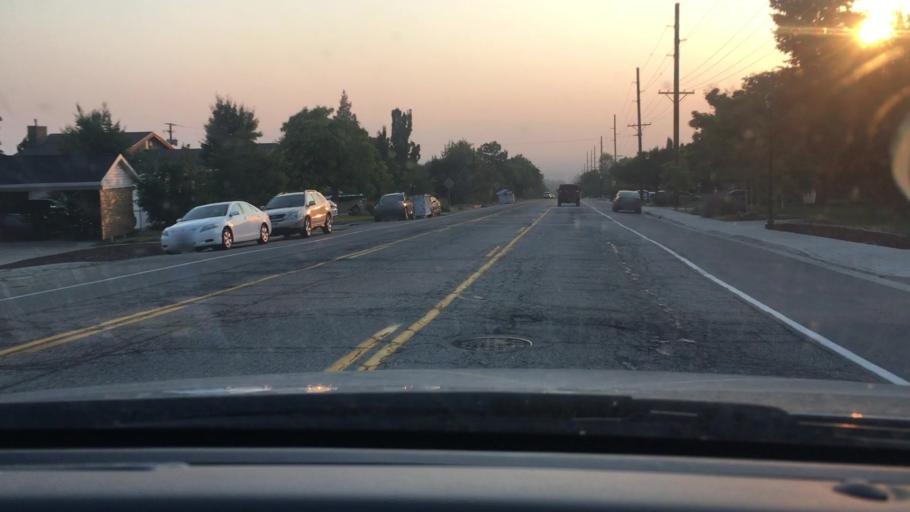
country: US
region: Utah
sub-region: Salt Lake County
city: Mount Olympus
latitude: 40.6871
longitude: -111.8022
